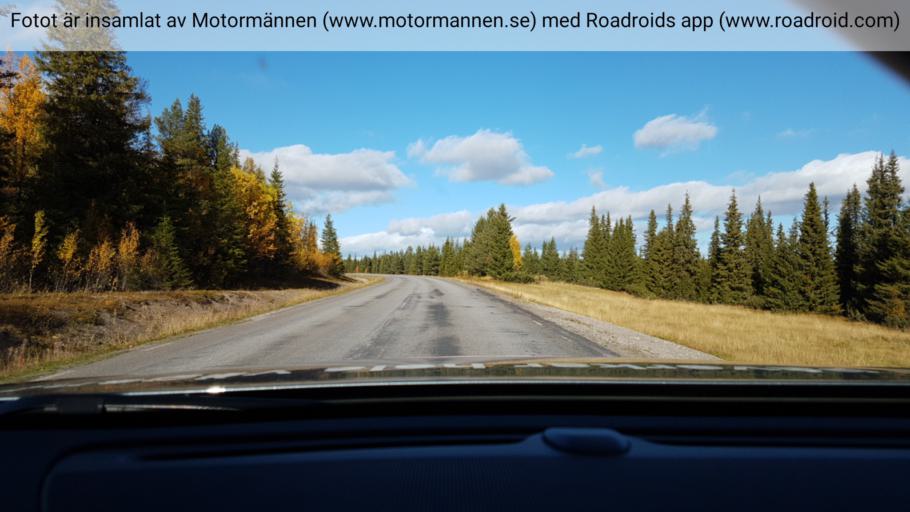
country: SE
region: Norrbotten
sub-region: Arjeplogs Kommun
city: Arjeplog
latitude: 65.9036
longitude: 18.3596
